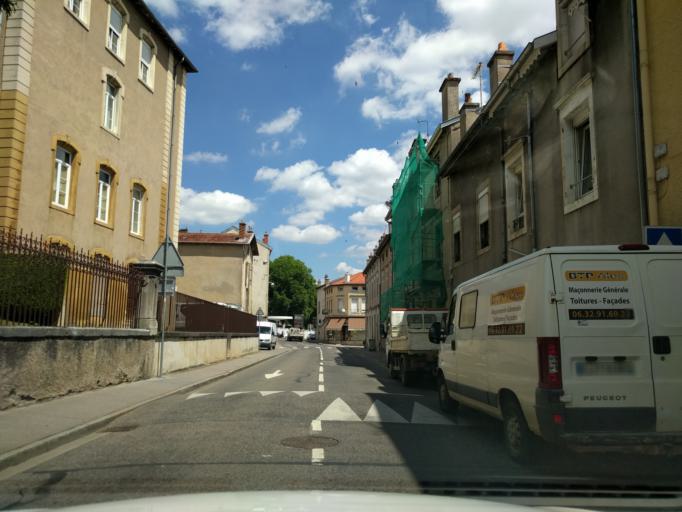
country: FR
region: Lorraine
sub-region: Departement de Meurthe-et-Moselle
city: Laxou
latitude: 48.6886
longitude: 6.1607
